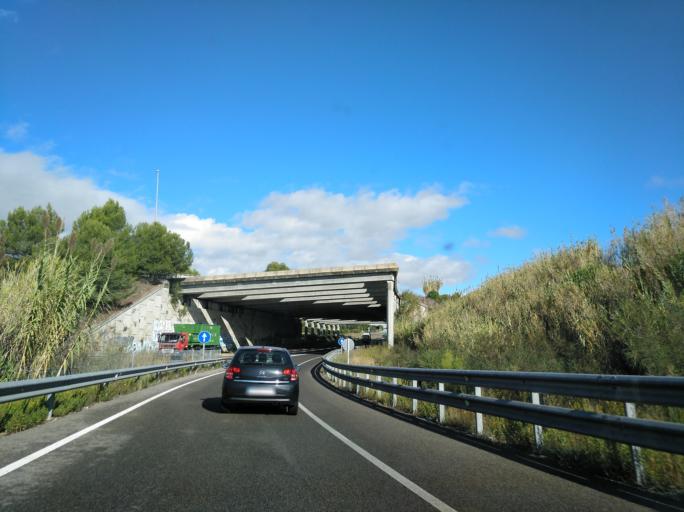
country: ES
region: Catalonia
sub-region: Provincia de Barcelona
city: Palafolls
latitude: 41.6721
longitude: 2.7269
